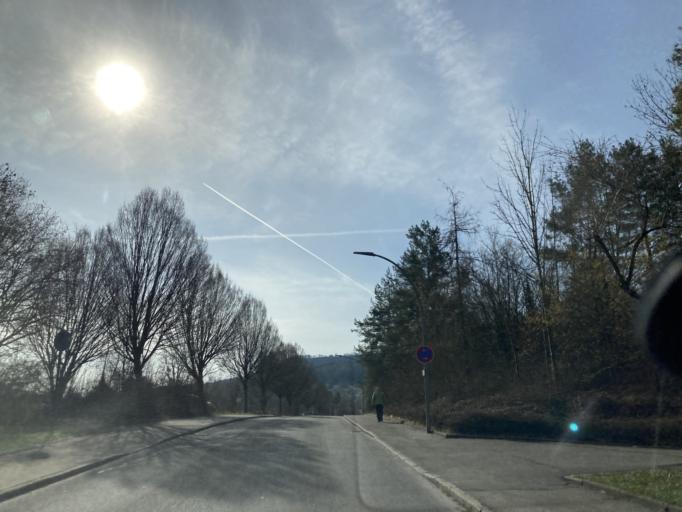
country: DE
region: Baden-Wuerttemberg
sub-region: Tuebingen Region
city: Mossingen
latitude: 48.4066
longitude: 9.0672
